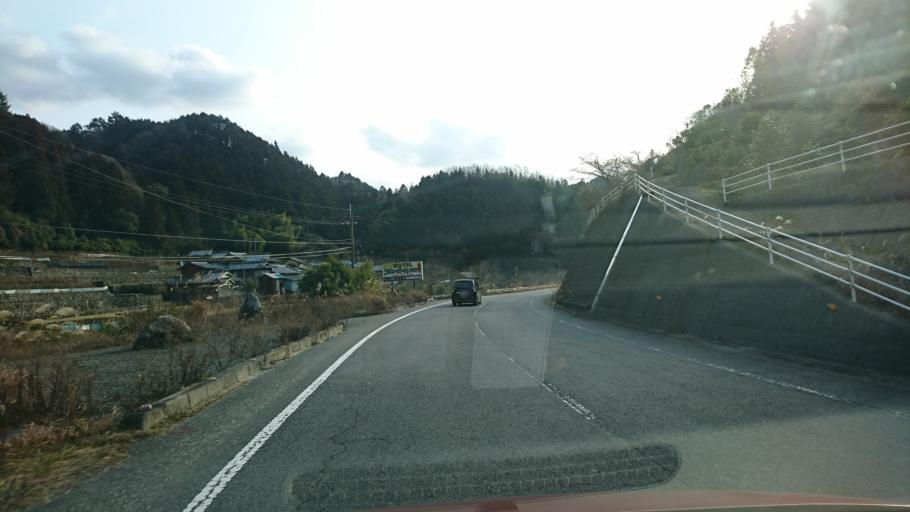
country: JP
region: Ehime
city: Hojo
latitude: 33.9191
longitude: 132.8859
